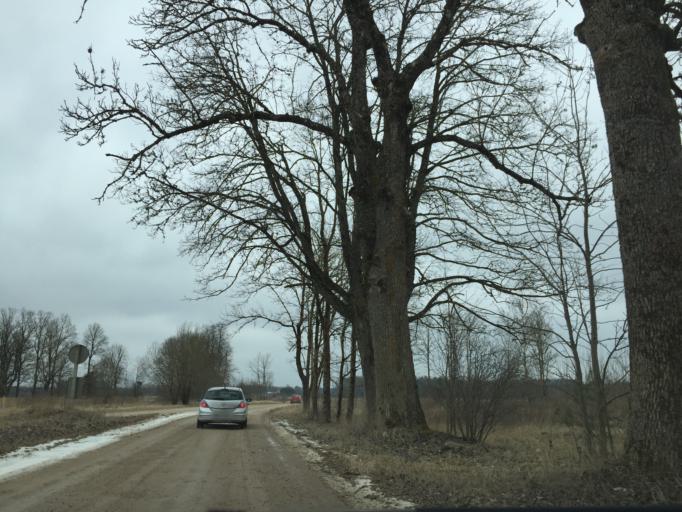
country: LV
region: Kegums
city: Kegums
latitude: 56.7684
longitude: 24.7724
